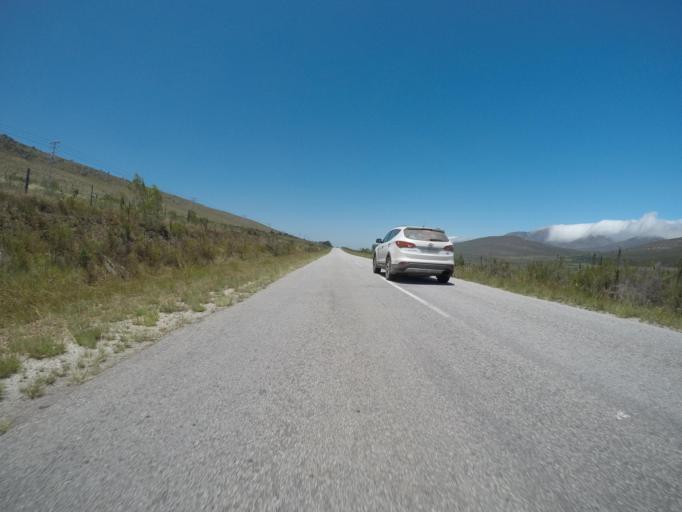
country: ZA
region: Eastern Cape
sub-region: Cacadu District Municipality
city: Kareedouw
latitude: -33.8426
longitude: 23.9402
